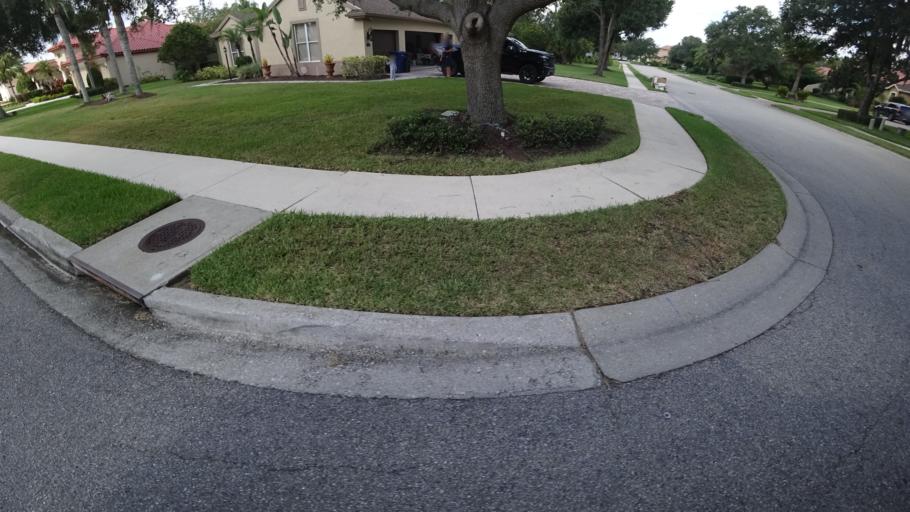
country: US
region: Florida
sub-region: Sarasota County
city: The Meadows
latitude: 27.4096
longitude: -82.4333
